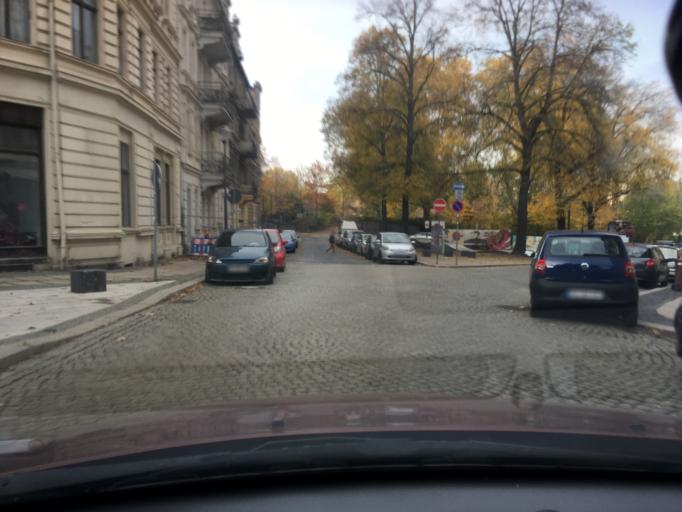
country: DE
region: Saxony
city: Goerlitz
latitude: 51.1524
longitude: 14.9754
